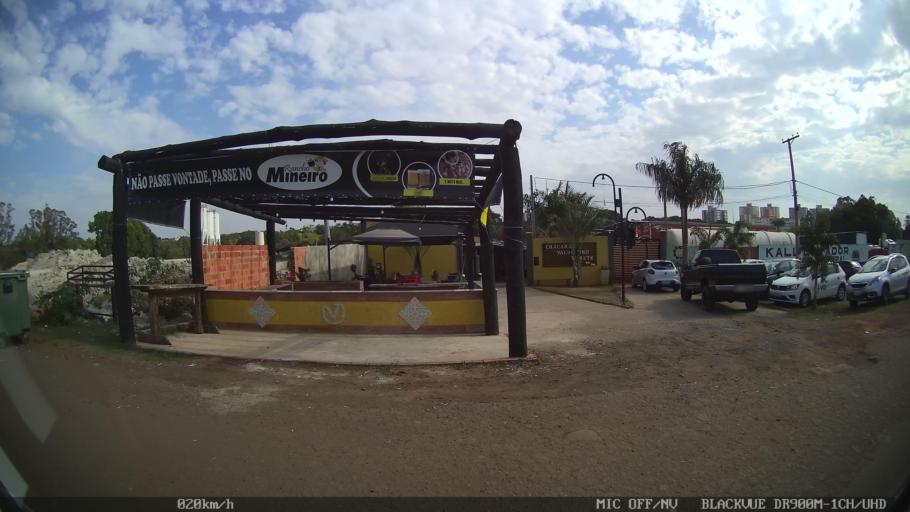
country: BR
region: Sao Paulo
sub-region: Paulinia
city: Paulinia
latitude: -22.7598
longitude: -47.1445
